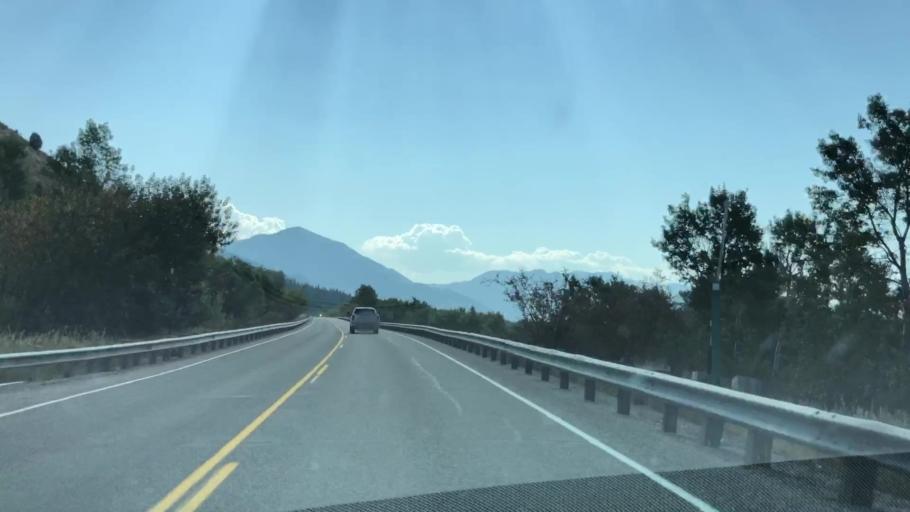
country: US
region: Wyoming
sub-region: Teton County
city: Hoback
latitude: 43.2084
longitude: -111.0565
